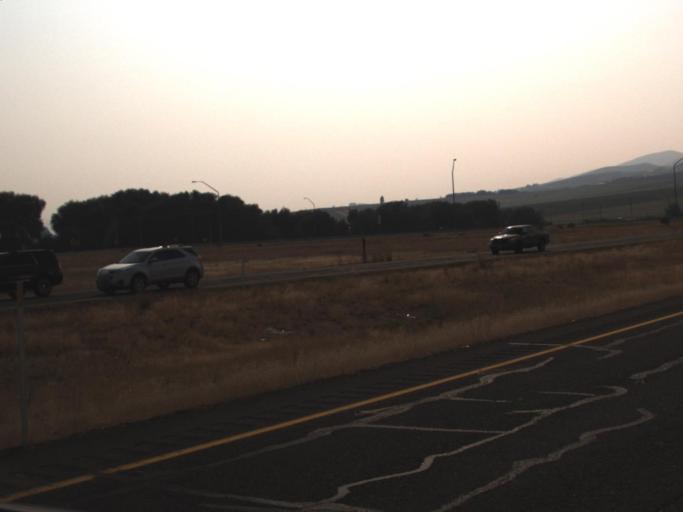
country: US
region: Washington
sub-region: Kittitas County
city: Ellensburg
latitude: 46.9294
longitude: -120.5012
